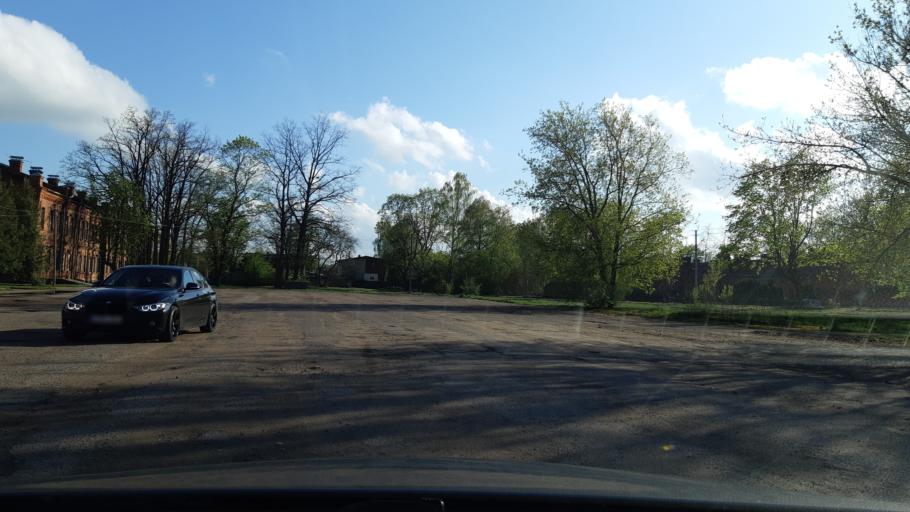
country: LT
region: Kauno apskritis
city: Dainava (Kaunas)
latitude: 54.8678
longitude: 23.9663
